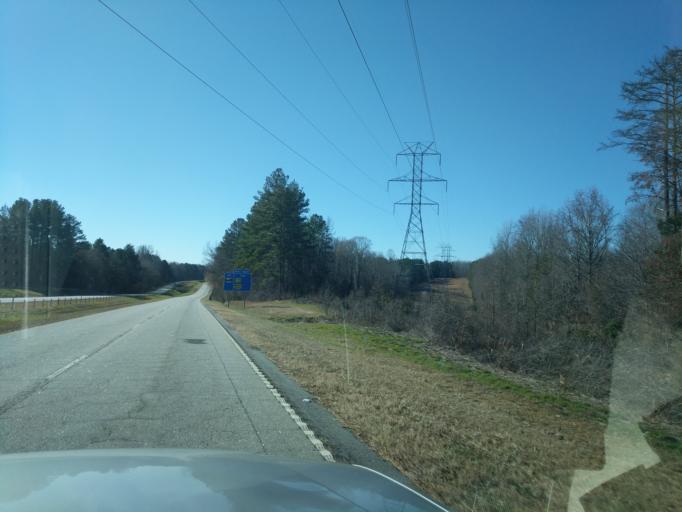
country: US
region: South Carolina
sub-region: Pickens County
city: Central
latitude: 34.7173
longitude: -82.7463
